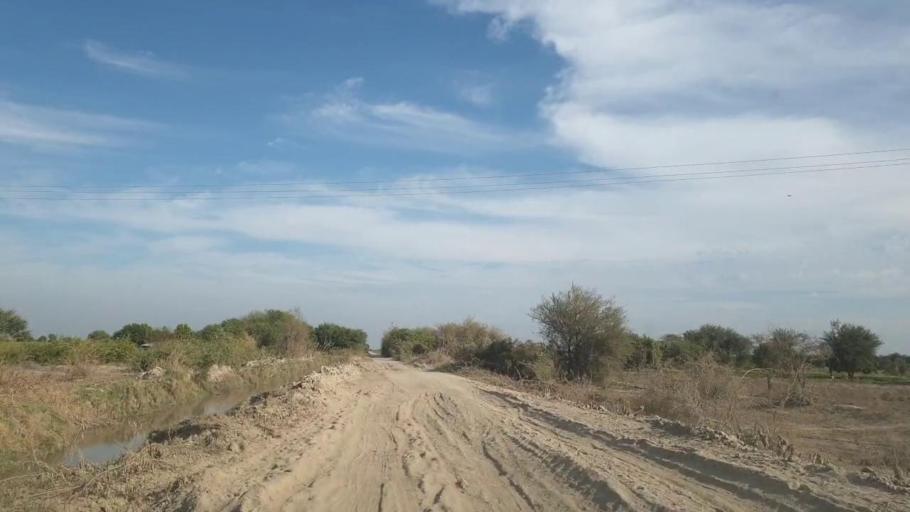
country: PK
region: Sindh
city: Pithoro
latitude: 25.6437
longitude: 69.3682
